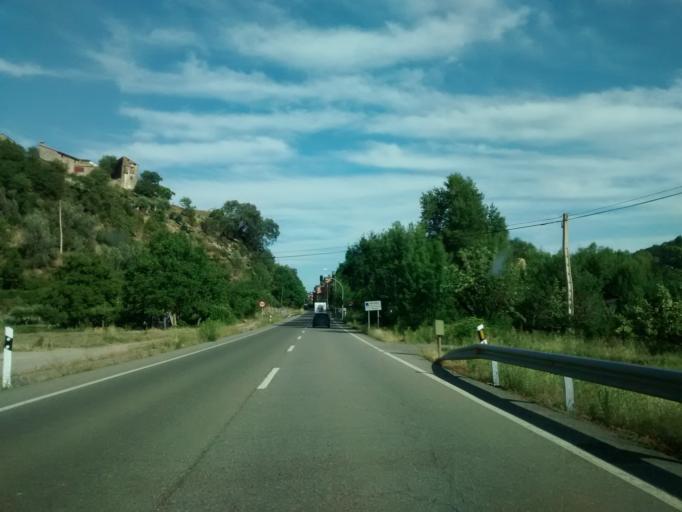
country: ES
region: Aragon
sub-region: Provincia de Huesca
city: Boltana
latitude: 42.4459
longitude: 0.0640
